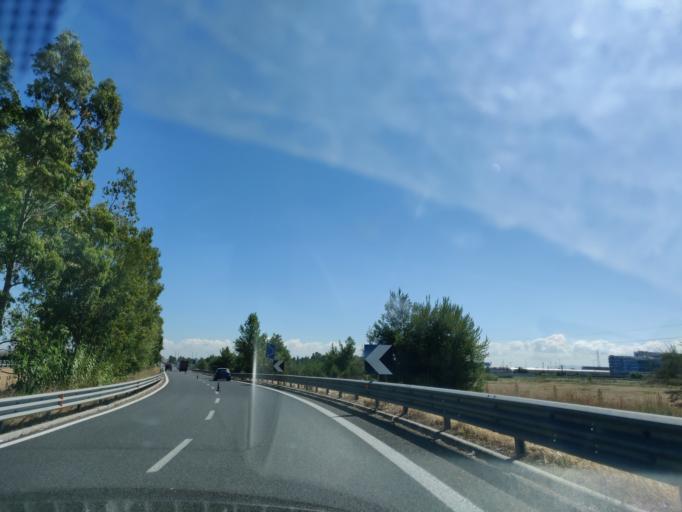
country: IT
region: Latium
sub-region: Citta metropolitana di Roma Capitale
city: Npp 23 (Parco Leonardo)
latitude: 41.8092
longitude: 12.3127
